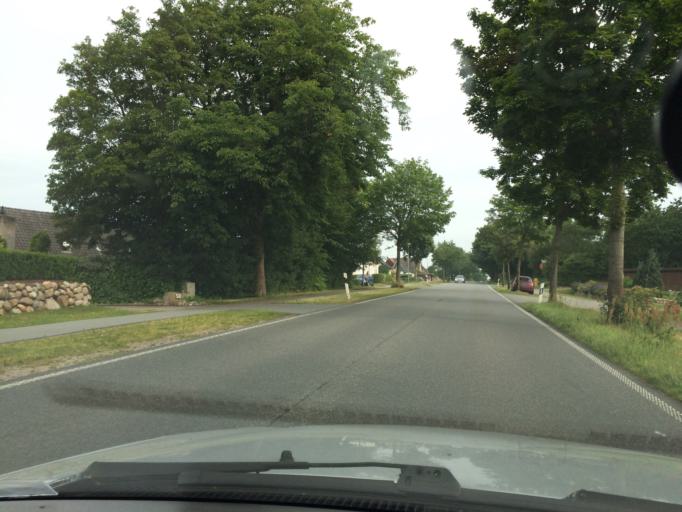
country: DE
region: Schleswig-Holstein
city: Jarplund-Weding
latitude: 54.7467
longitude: 9.4377
